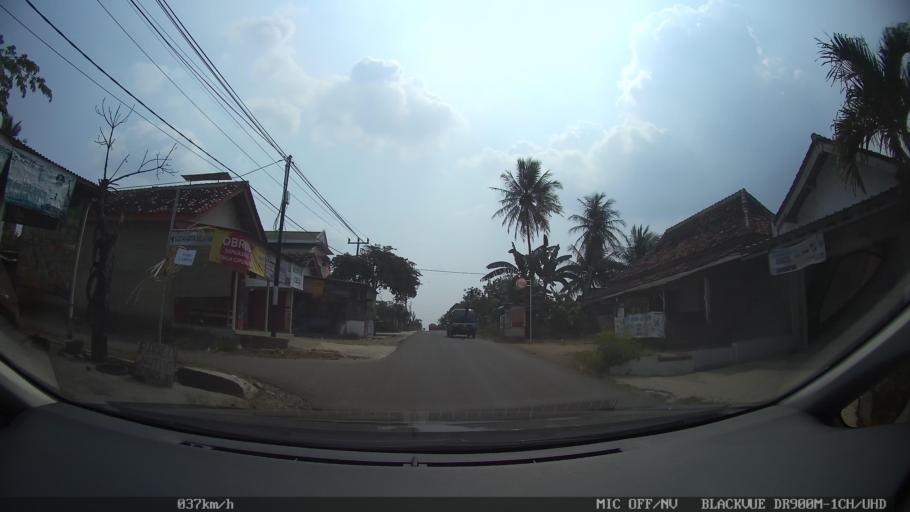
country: ID
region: Lampung
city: Gadingrejo
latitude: -5.3497
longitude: 105.0268
